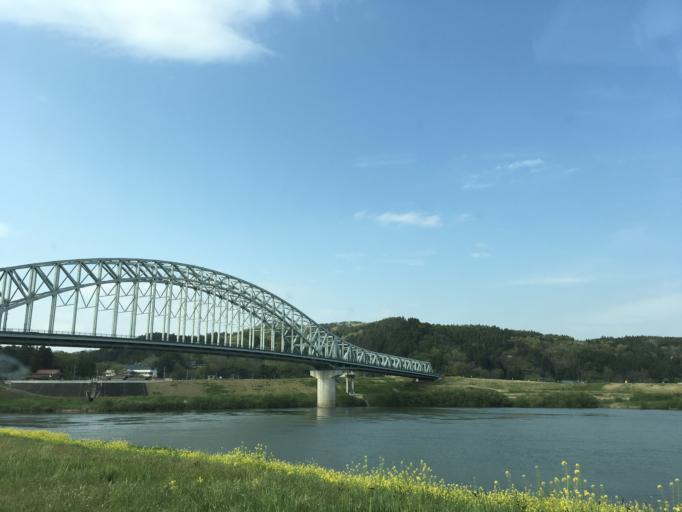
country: JP
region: Iwate
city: Ichinoseki
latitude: 38.8964
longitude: 141.2630
